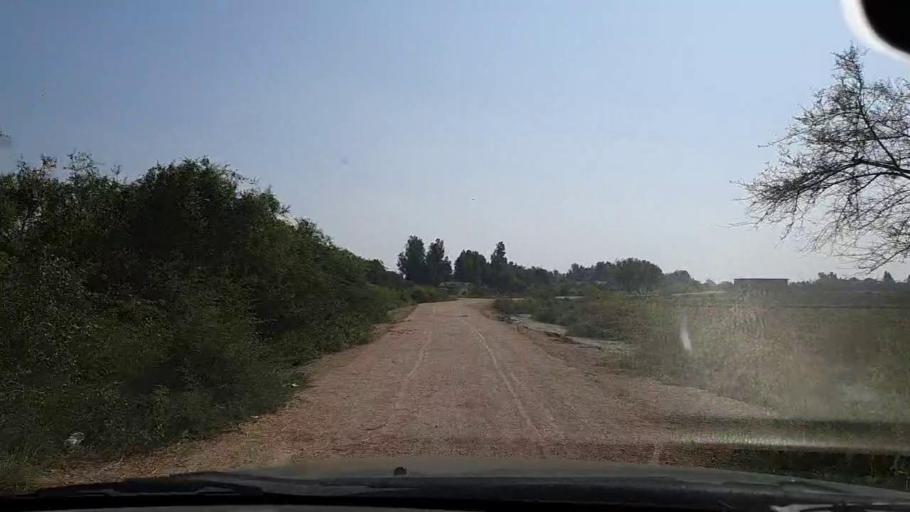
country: PK
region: Sindh
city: Chuhar Jamali
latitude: 24.3981
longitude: 67.8239
